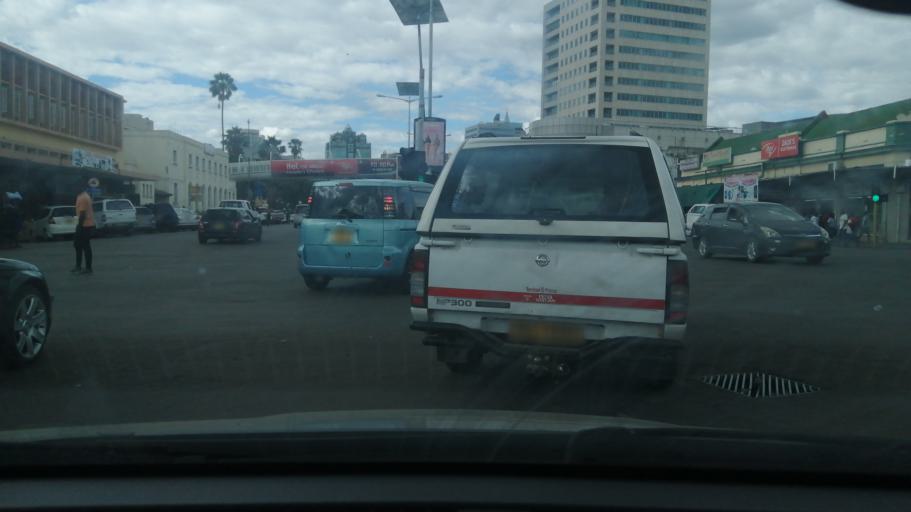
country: ZW
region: Harare
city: Harare
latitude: -17.8334
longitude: 31.0467
